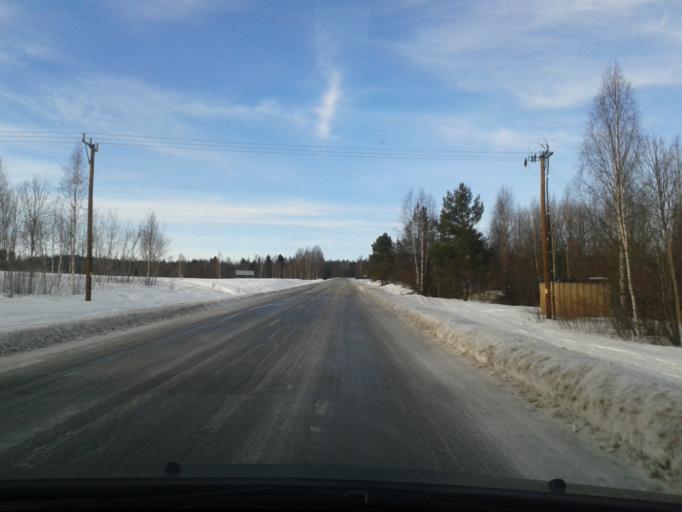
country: SE
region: Vaesternorrland
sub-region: OErnskoeldsviks Kommun
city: Bredbyn
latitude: 63.5716
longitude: 17.9274
